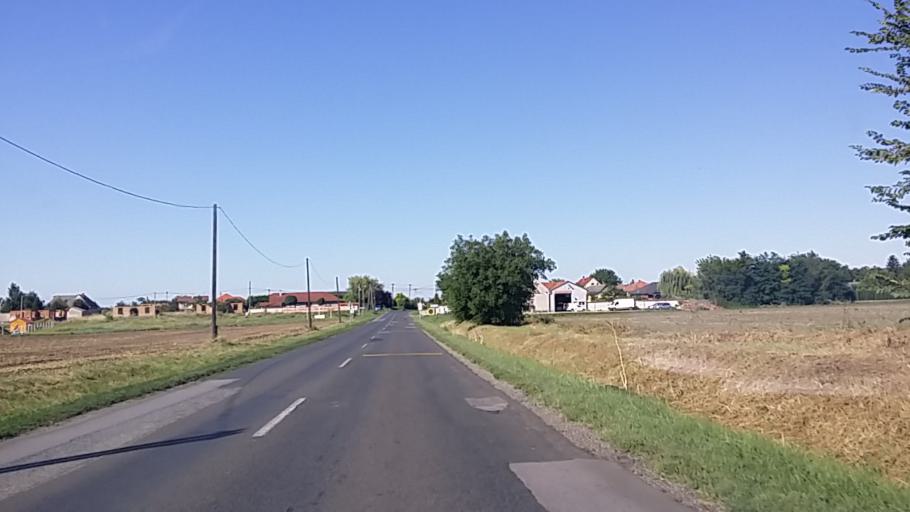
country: HU
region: Fejer
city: dunaujvaros
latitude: 46.9608
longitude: 18.8754
